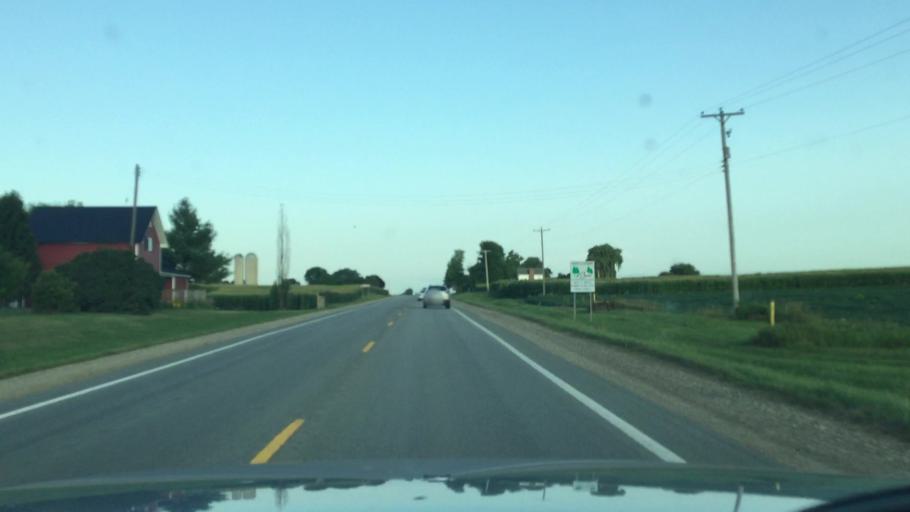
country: US
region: Michigan
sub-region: Gratiot County
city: Ithaca
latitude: 43.1760
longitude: -84.6401
